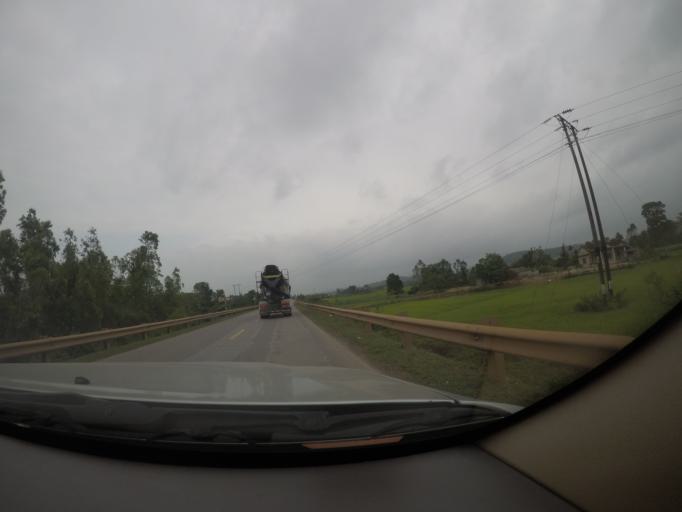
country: VN
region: Quang Binh
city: Kien Giang
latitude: 17.2483
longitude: 106.6827
